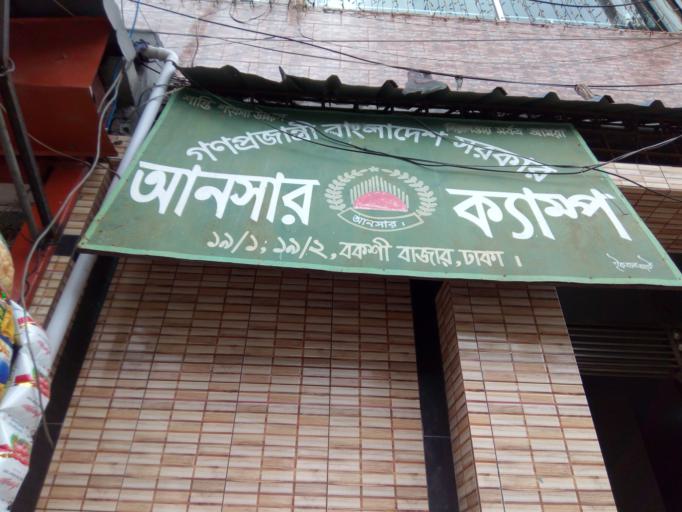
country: BD
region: Dhaka
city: Azimpur
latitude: 23.7244
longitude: 90.3953
